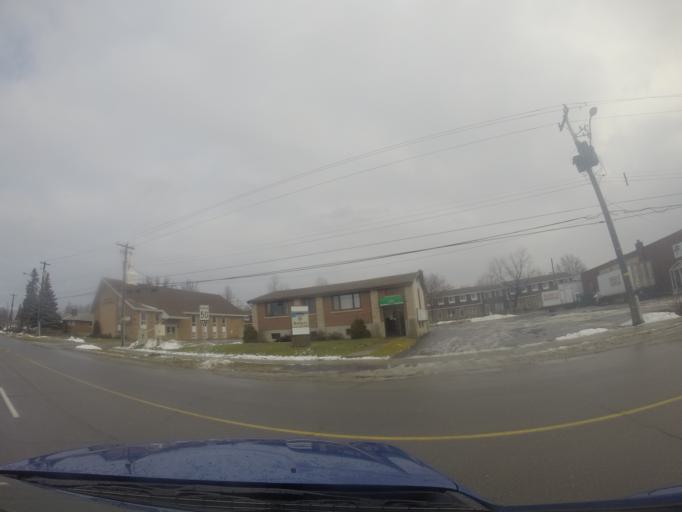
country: CA
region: Ontario
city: Greater Sudbury
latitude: 46.5227
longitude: -80.9293
